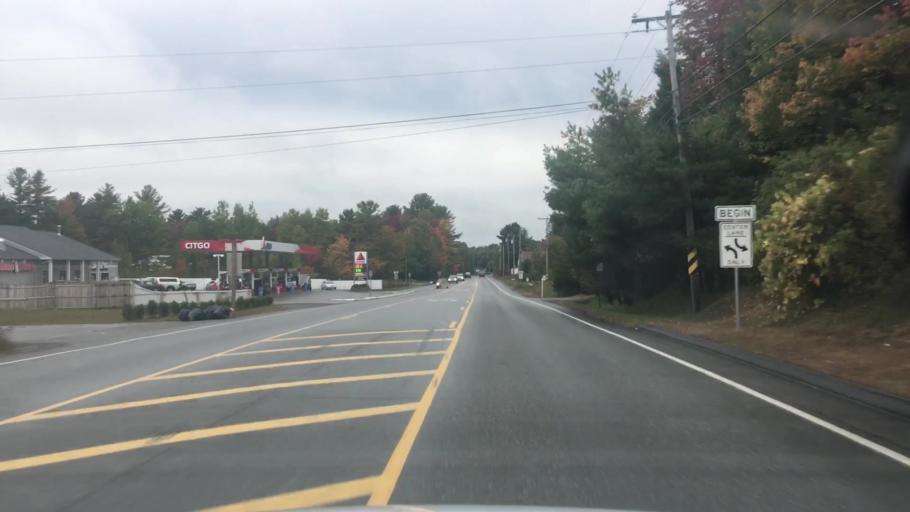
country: US
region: Maine
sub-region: Kennebec County
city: Augusta
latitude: 44.3743
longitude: -69.7958
